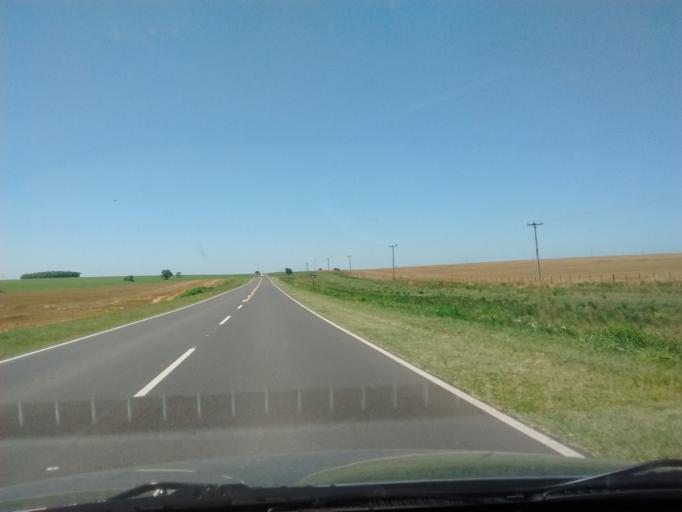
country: AR
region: Entre Rios
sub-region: Departamento de Victoria
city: Victoria
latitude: -32.7914
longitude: -59.8993
